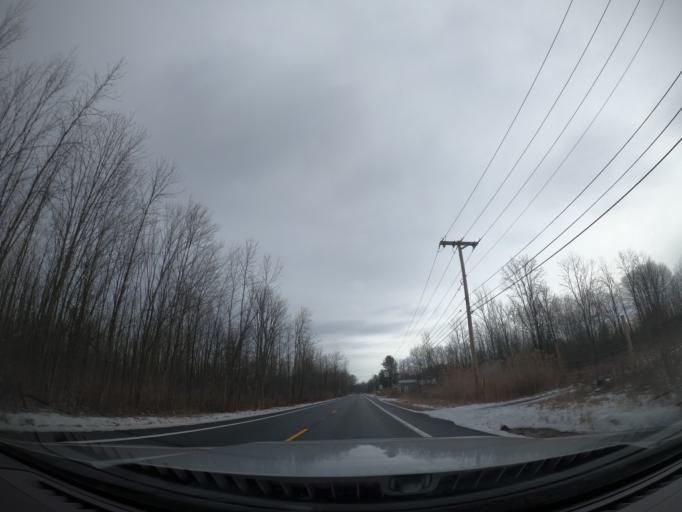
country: US
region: New York
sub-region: Madison County
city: Bridgeport
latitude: 43.1393
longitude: -75.9817
